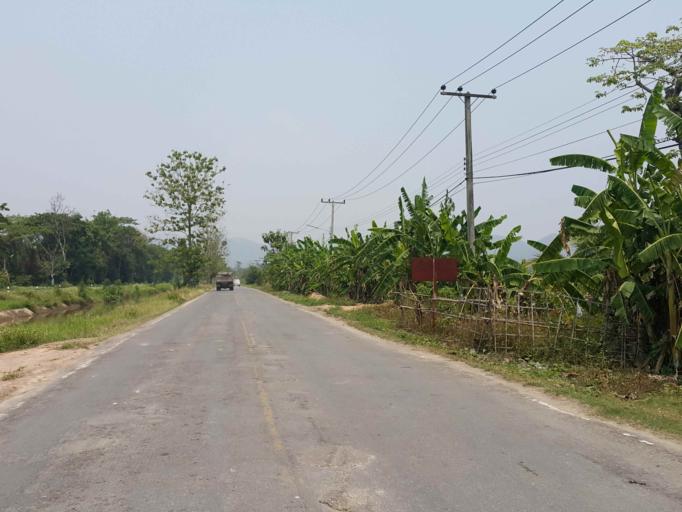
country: TH
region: Chiang Mai
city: San Sai
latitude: 18.8857
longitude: 99.0818
